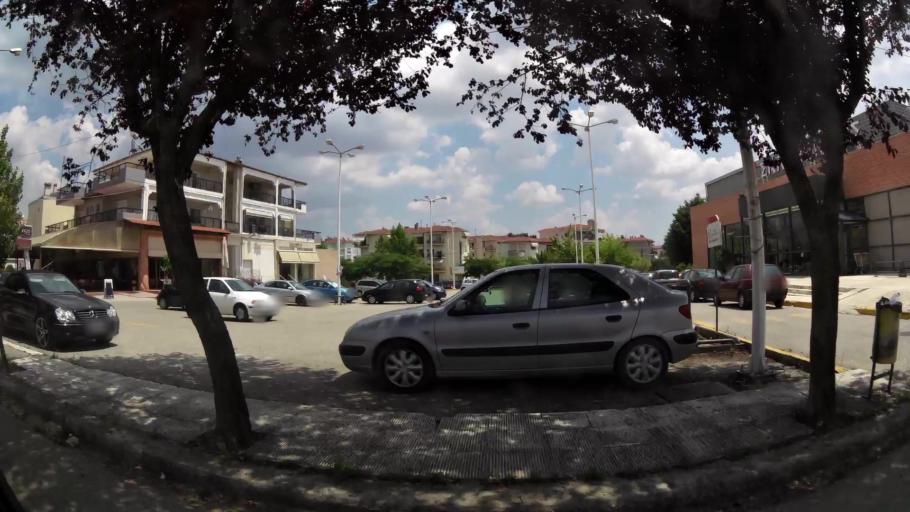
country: GR
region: West Macedonia
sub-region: Nomos Kozanis
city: Kozani
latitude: 40.2928
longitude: 21.7832
